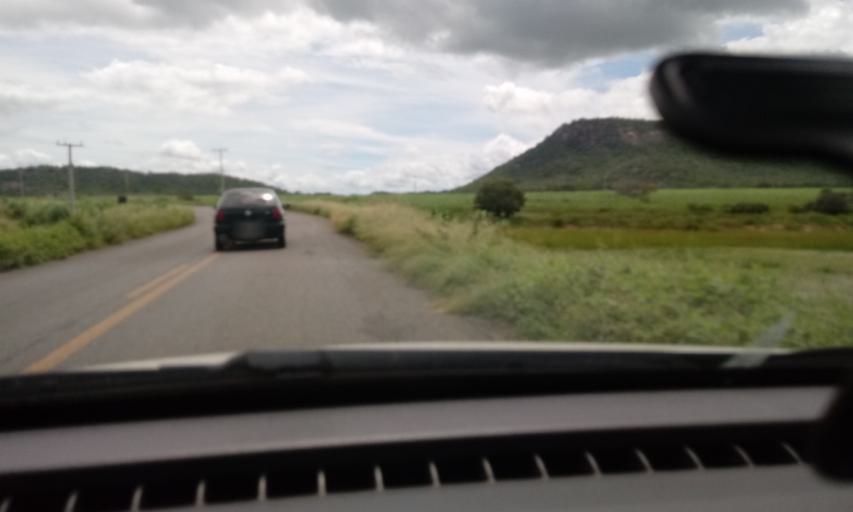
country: BR
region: Bahia
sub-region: Guanambi
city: Guanambi
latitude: -14.1469
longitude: -42.8315
